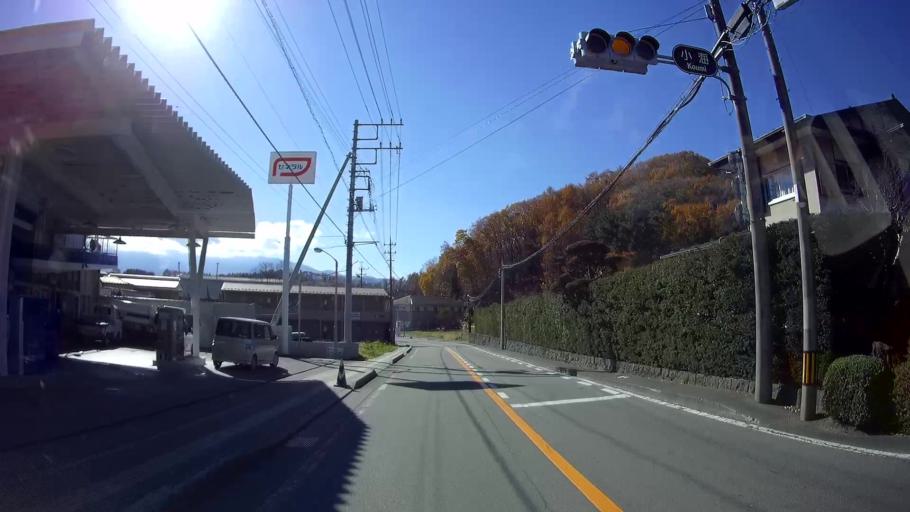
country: JP
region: Yamanashi
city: Fujikawaguchiko
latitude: 35.5031
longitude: 138.7378
